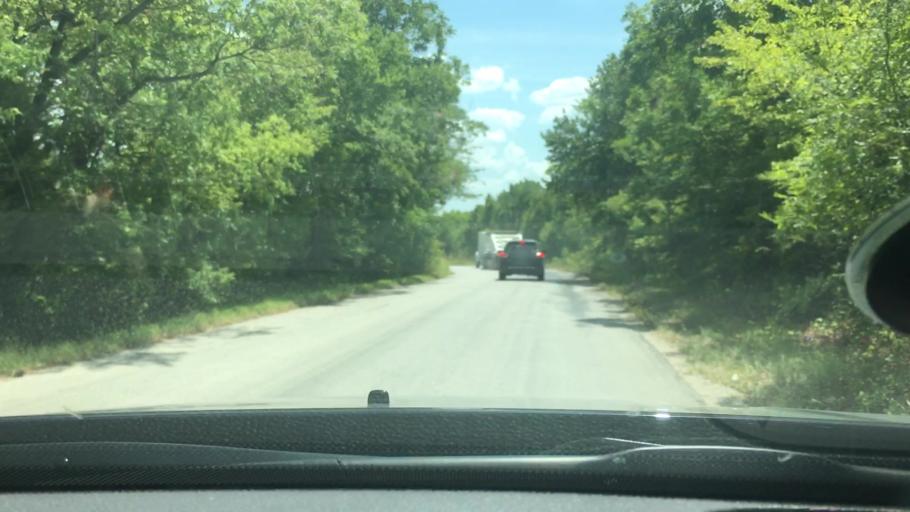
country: US
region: Oklahoma
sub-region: Carter County
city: Ardmore
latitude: 34.0787
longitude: -97.1544
